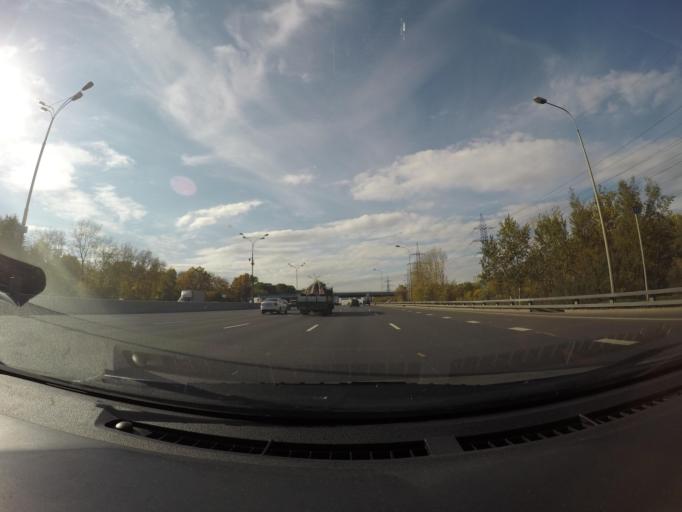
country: RU
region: Moscow
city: Vagonoremont
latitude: 55.9105
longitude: 37.5669
